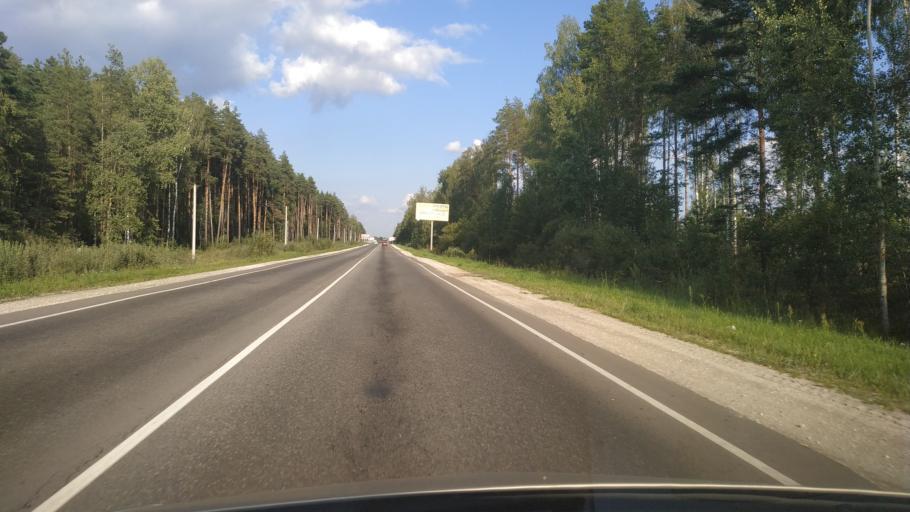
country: RU
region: Moskovskaya
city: Shaturtorf
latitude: 55.5785
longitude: 39.4438
